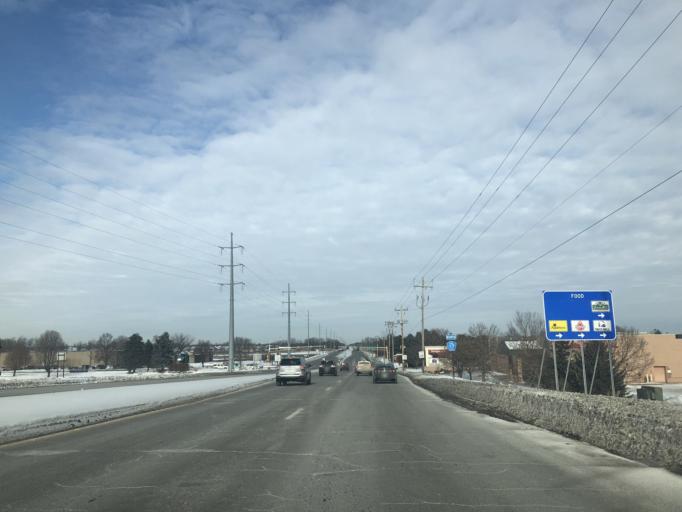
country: US
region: Minnesota
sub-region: Anoka County
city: Circle Pines
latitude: 45.1607
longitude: -93.1632
